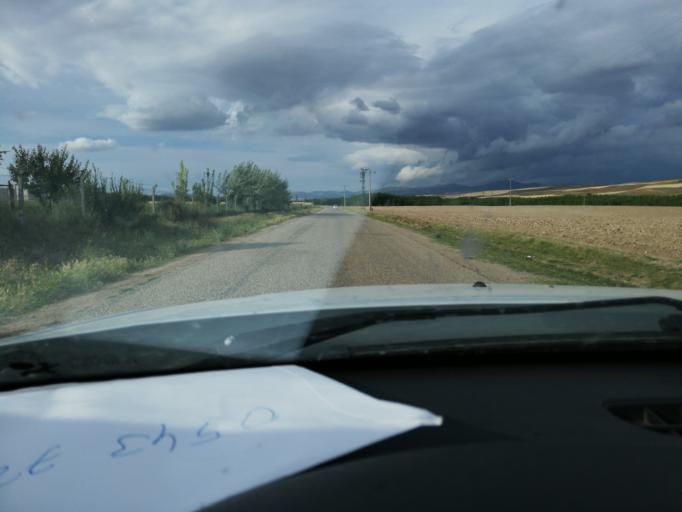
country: TR
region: Kirsehir
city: Kirsehir
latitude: 39.0181
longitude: 34.1210
